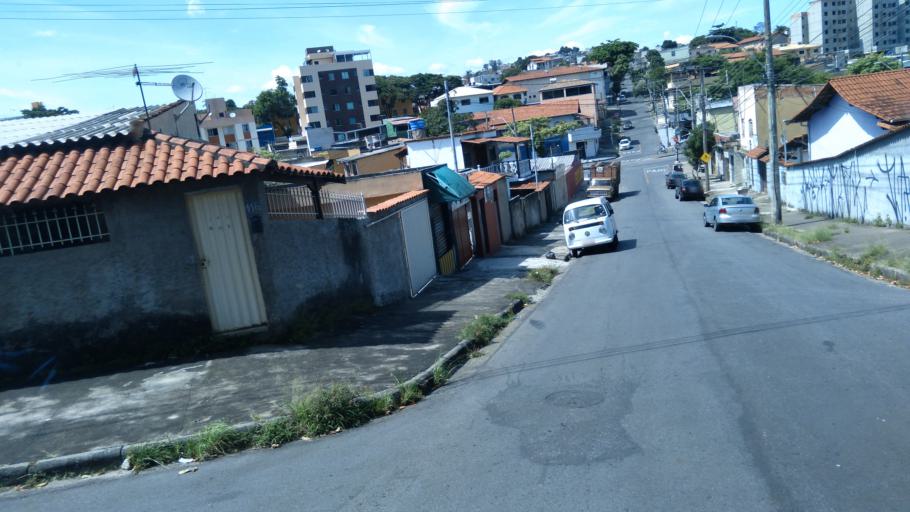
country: BR
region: Minas Gerais
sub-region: Contagem
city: Contagem
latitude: -19.8951
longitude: -44.0136
